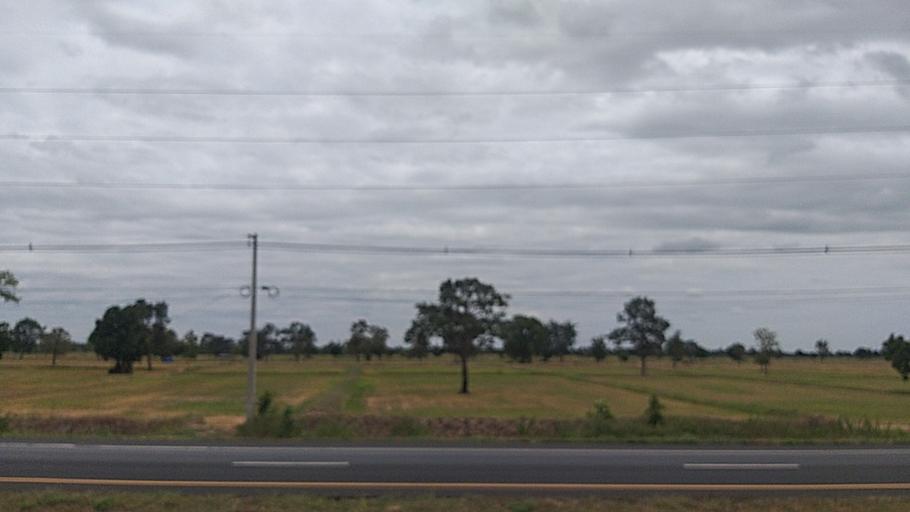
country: TH
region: Buriram
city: Chaloem Phra Kiat
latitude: 14.6070
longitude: 102.9762
